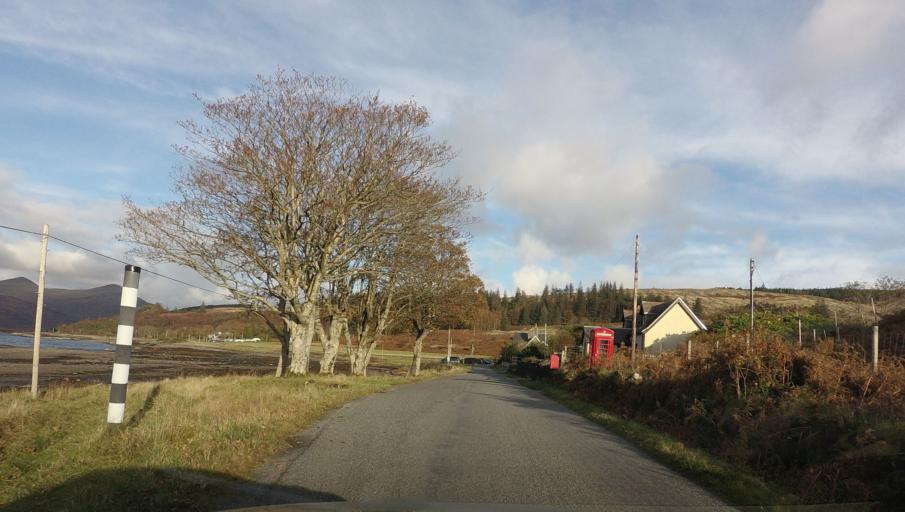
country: GB
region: Scotland
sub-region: Argyll and Bute
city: Isle Of Mull
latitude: 56.3643
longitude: -6.0221
